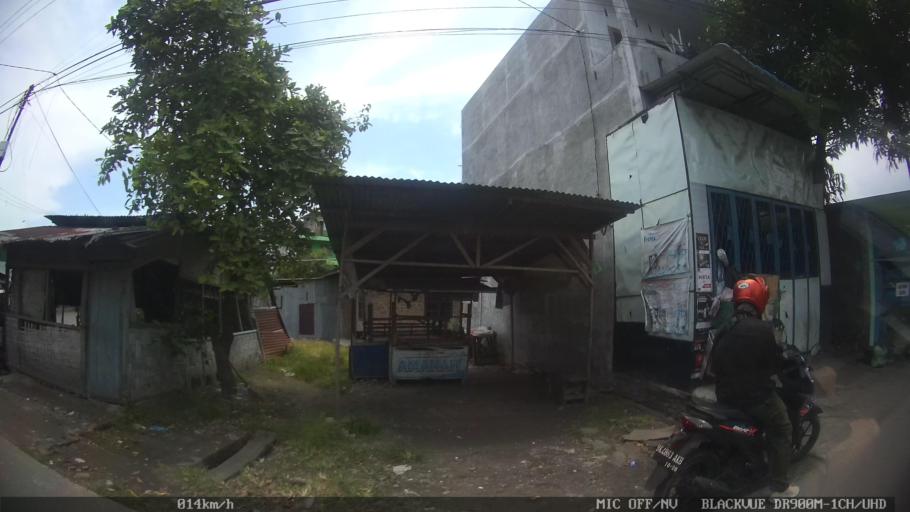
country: ID
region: North Sumatra
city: Labuhan Deli
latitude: 3.6841
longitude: 98.6900
